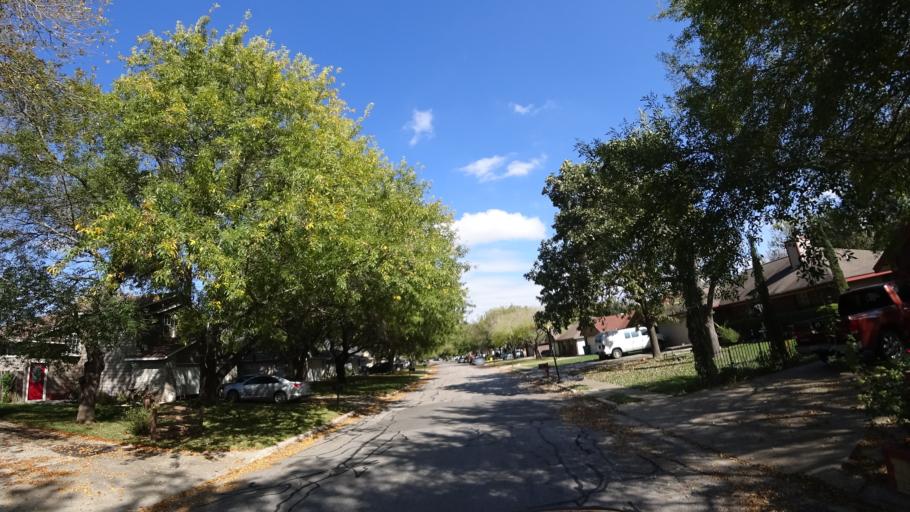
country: US
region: Texas
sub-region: Travis County
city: Windemere
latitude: 30.4502
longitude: -97.6440
